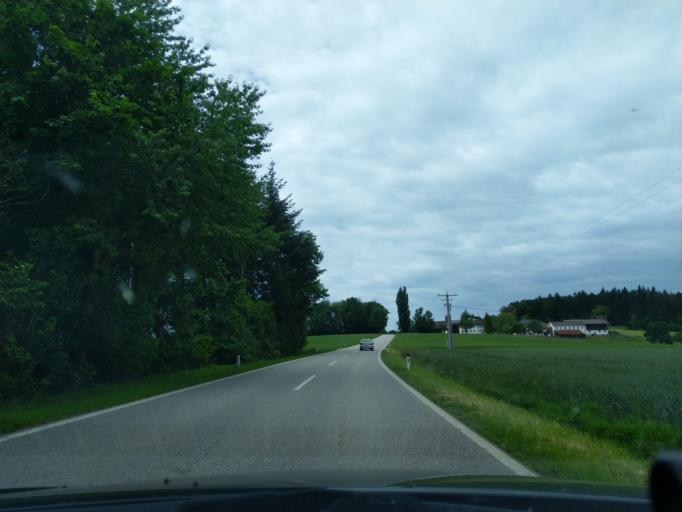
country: AT
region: Upper Austria
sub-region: Politischer Bezirk Ried im Innkreis
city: Ried im Innkreis
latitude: 48.2846
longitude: 13.4163
